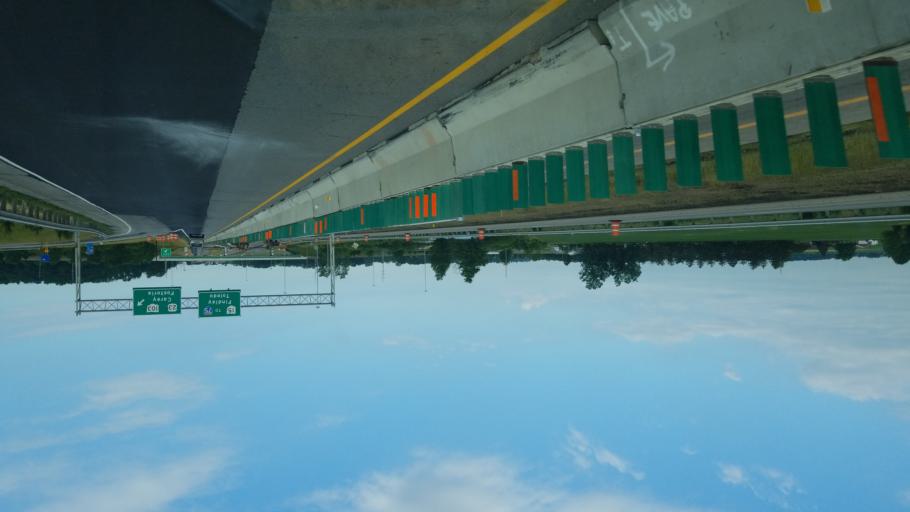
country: US
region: Ohio
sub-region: Wyandot County
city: Carey
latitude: 40.9391
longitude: -83.3963
